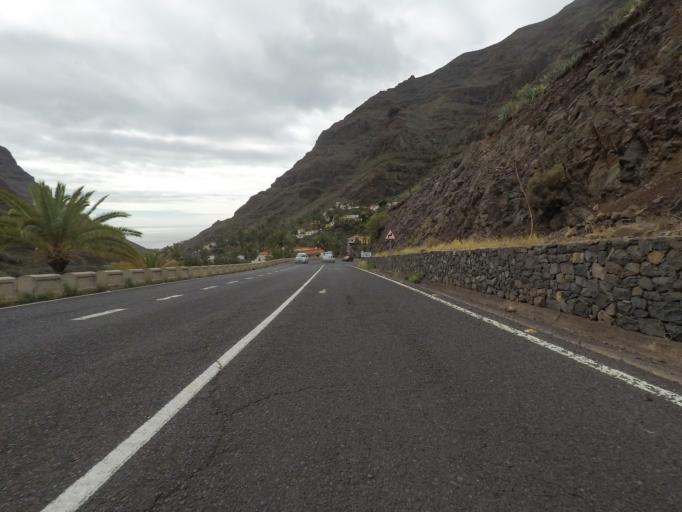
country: ES
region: Canary Islands
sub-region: Provincia de Santa Cruz de Tenerife
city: Vallehermosa
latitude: 28.1085
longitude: -17.3238
